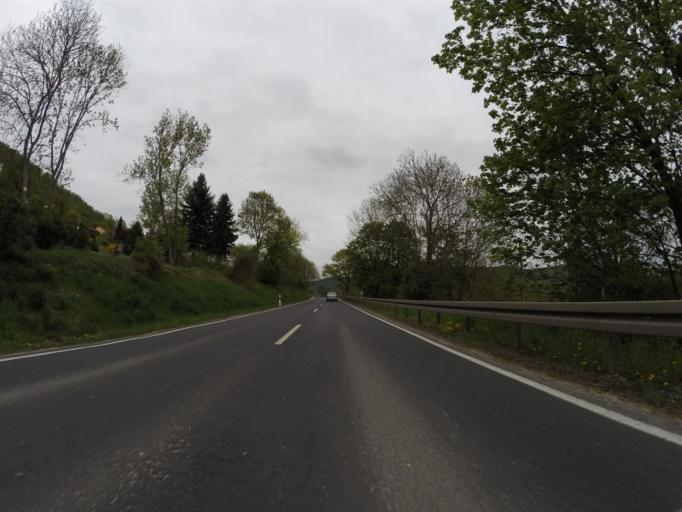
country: DE
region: Thuringia
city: Neuengonna
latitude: 50.9804
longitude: 11.6516
